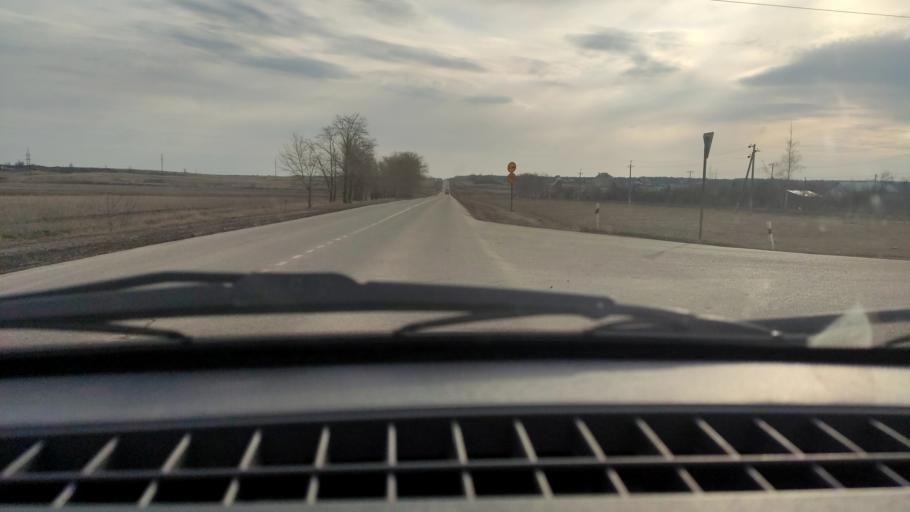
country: RU
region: Bashkortostan
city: Davlekanovo
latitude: 54.2349
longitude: 55.0290
